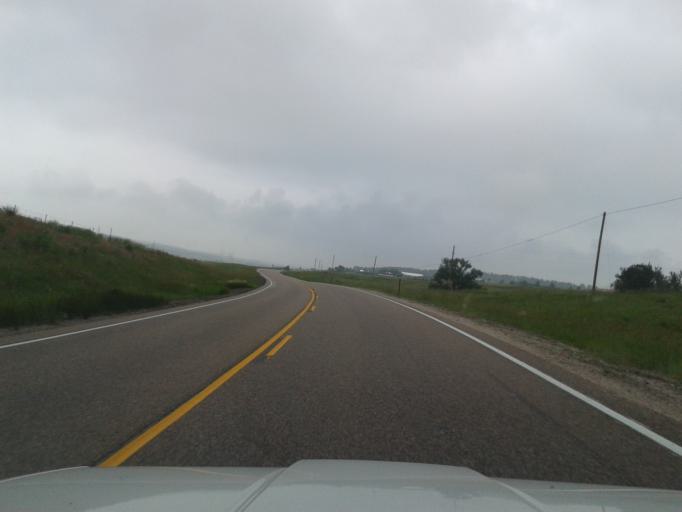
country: US
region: Colorado
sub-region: El Paso County
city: Woodmoor
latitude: 39.1681
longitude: -104.7429
